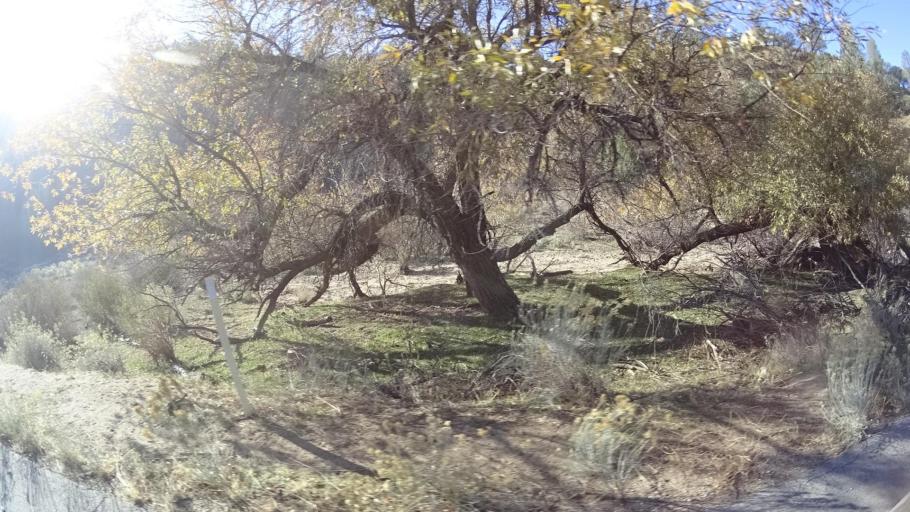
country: US
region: California
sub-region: Kern County
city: Golden Hills
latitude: 35.3065
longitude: -118.4318
